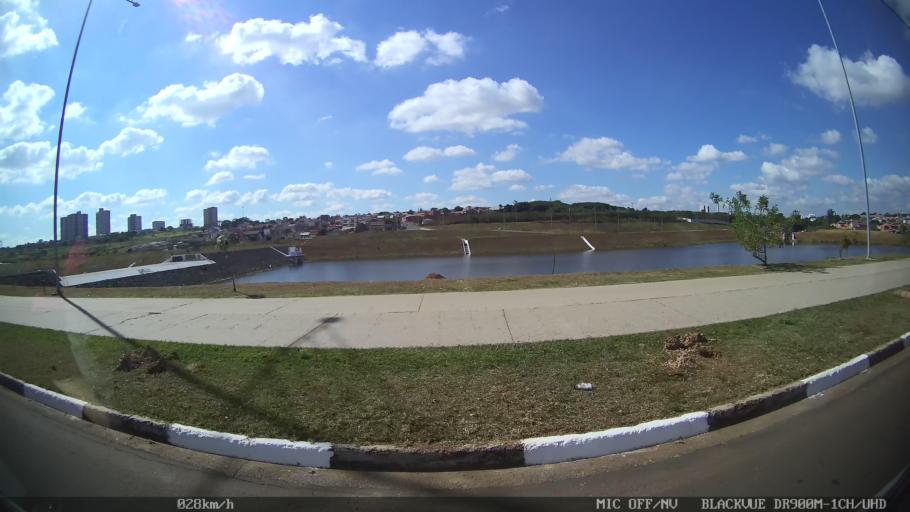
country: BR
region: Sao Paulo
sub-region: Hortolandia
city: Hortolandia
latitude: -22.8847
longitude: -47.2145
